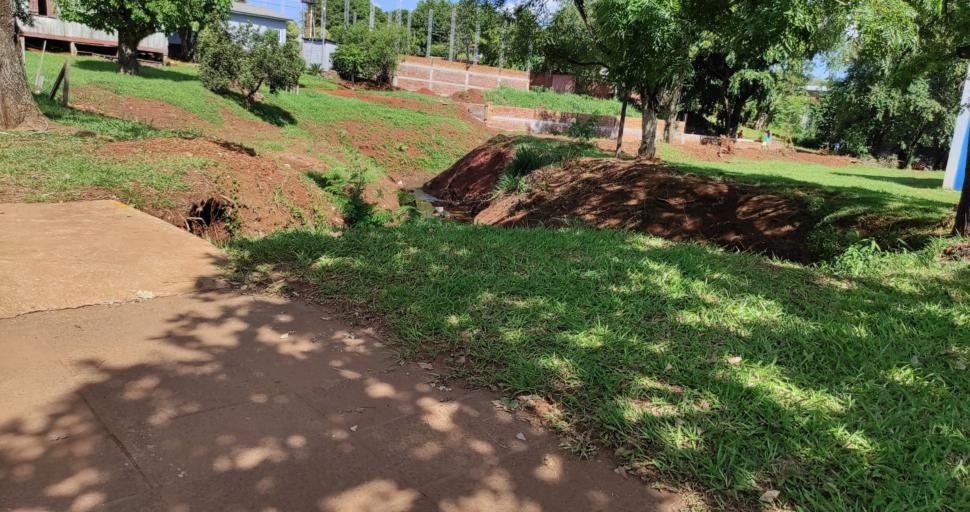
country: AR
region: Misiones
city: El Soberbio
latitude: -27.2979
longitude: -54.1956
